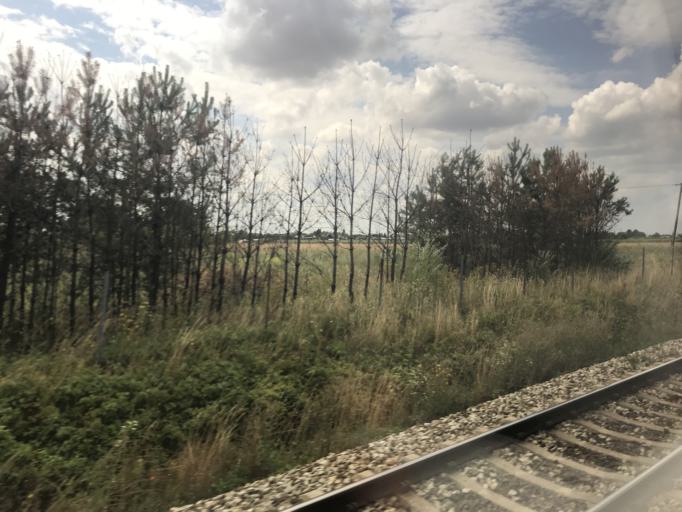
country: PL
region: Greater Poland Voivodeship
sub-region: Powiat poznanski
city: Buk
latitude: 52.3471
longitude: 16.5456
